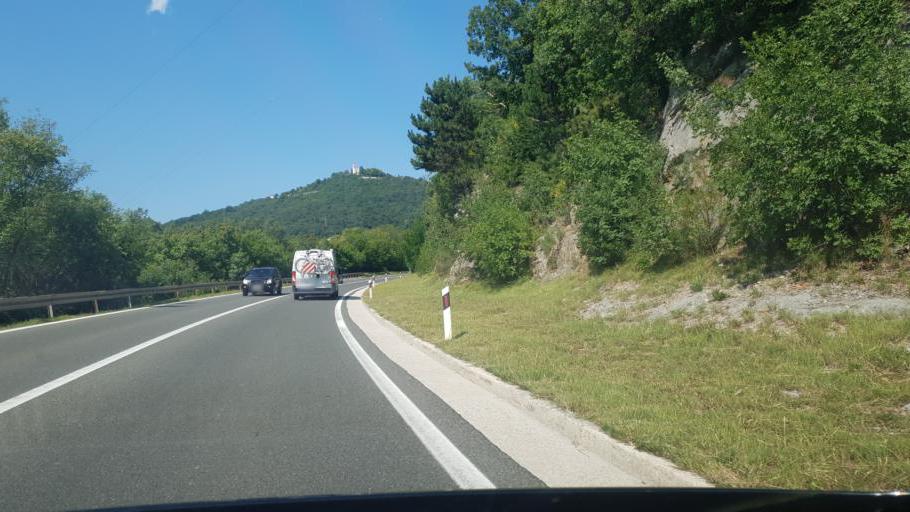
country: HR
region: Primorsko-Goranska
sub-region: Grad Opatija
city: Opatija
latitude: 45.3403
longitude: 14.2967
